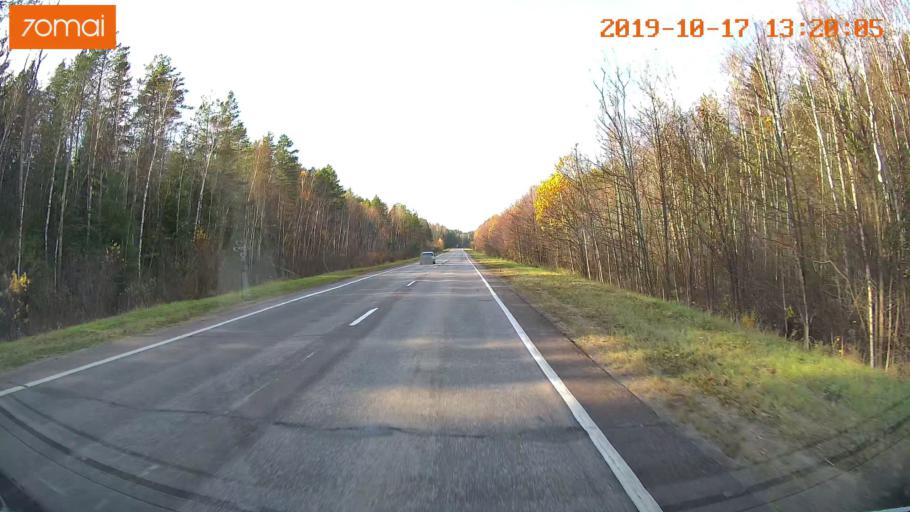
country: RU
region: Rjazan
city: Gus'-Zheleznyy
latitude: 55.0736
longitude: 41.0587
